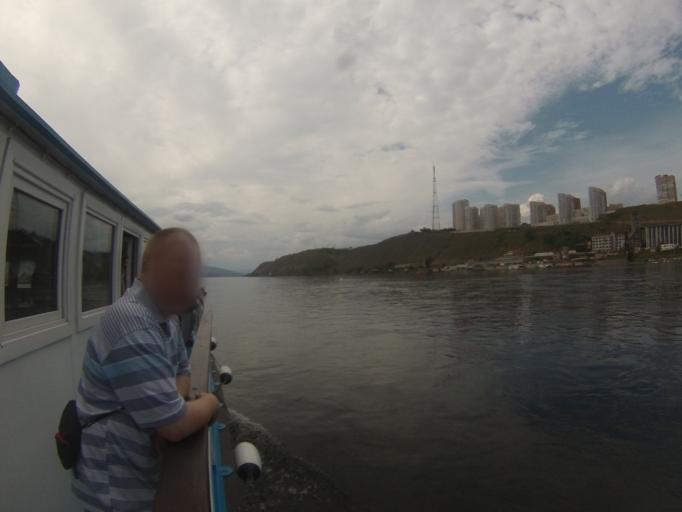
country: RU
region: Krasnoyarskiy
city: Krasnoyarsk
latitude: 55.9890
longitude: 92.8087
